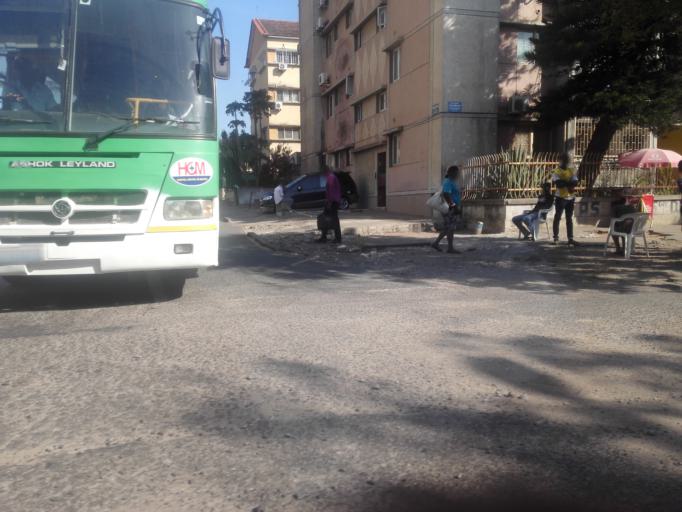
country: MZ
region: Maputo City
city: Maputo
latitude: -25.9564
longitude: 32.5862
